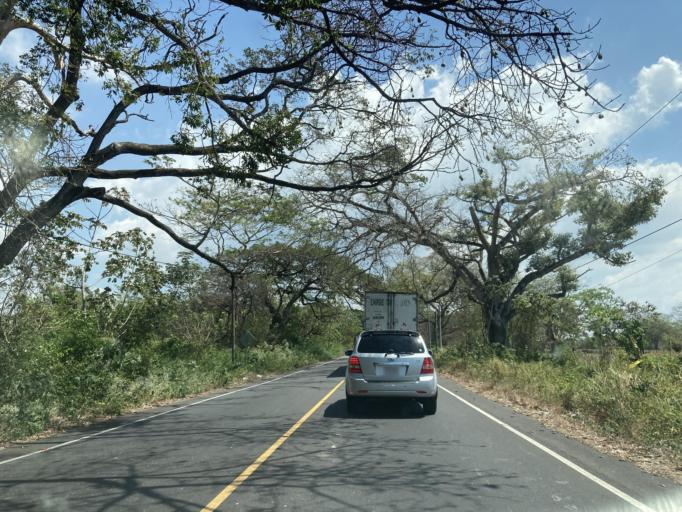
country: GT
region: Santa Rosa
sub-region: Municipio de Taxisco
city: Taxisco
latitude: 14.0915
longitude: -90.5624
